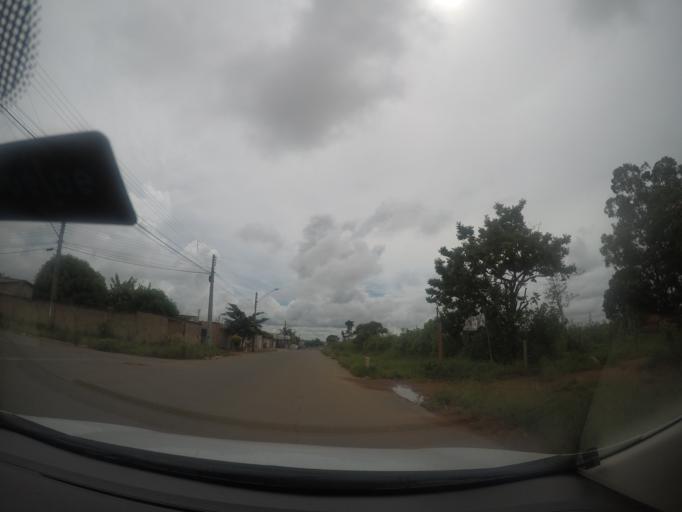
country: BR
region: Goias
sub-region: Trindade
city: Trindade
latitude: -16.6933
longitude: -49.4072
